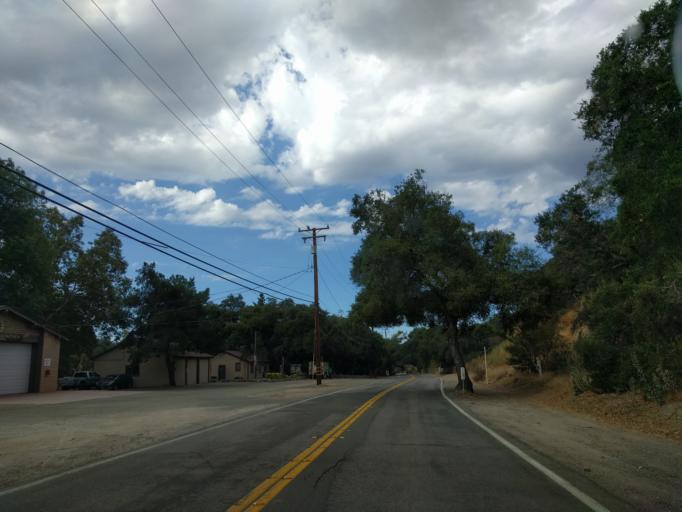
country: US
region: California
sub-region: Orange County
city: Trabuco Canyon
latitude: 33.6588
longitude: -117.5919
